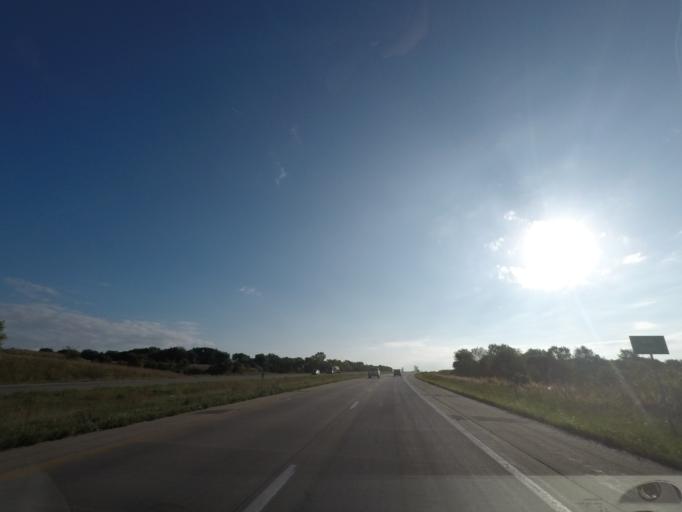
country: US
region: Iowa
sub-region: Warren County
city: Carlisle
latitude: 41.5112
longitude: -93.5517
